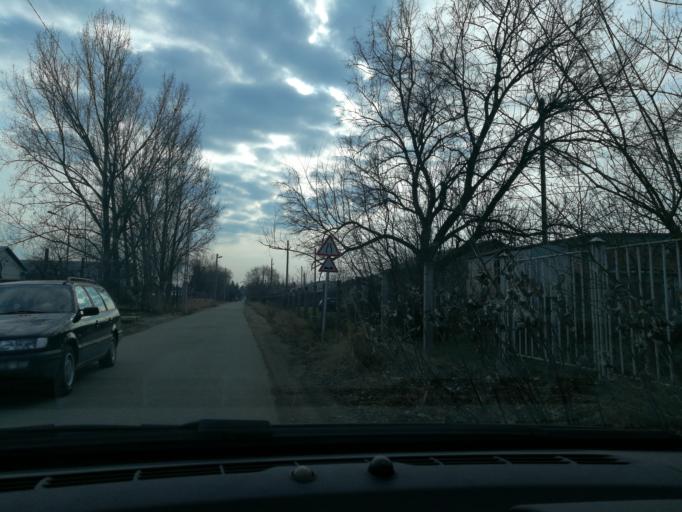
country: HU
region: Szabolcs-Szatmar-Bereg
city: Nyiregyhaza
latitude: 47.9332
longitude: 21.7215
